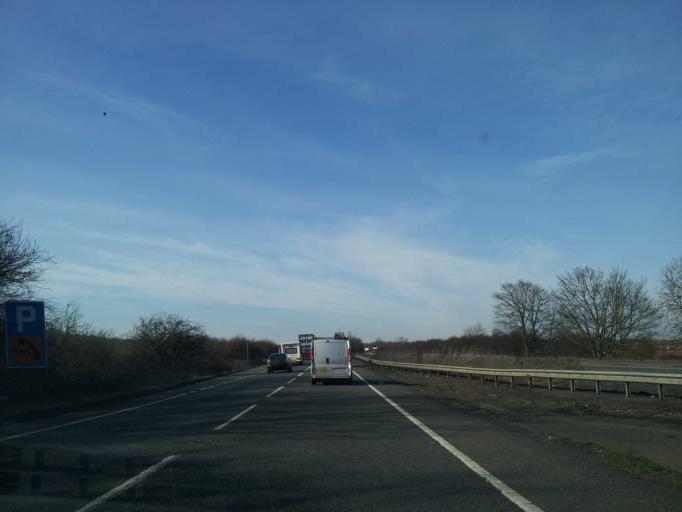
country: GB
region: England
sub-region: District of Rutland
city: Tickencote
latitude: 52.6788
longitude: -0.5404
